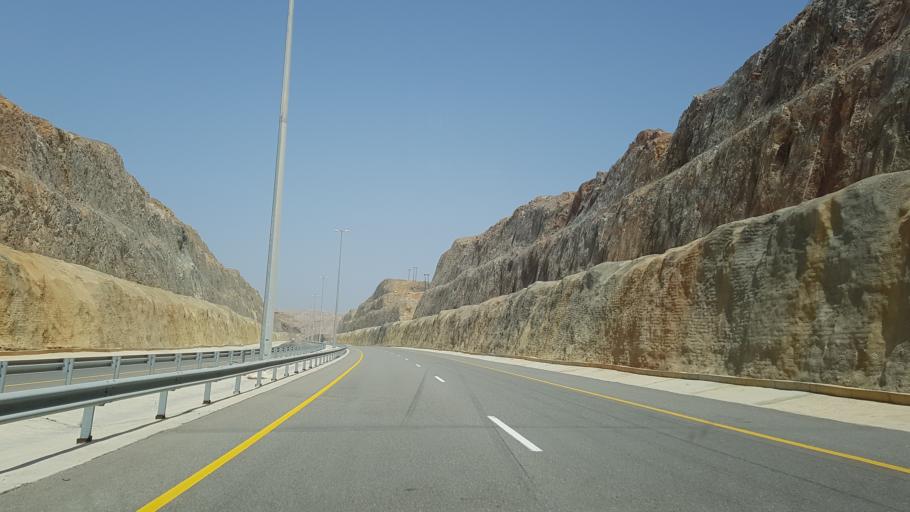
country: OM
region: Muhafazat Masqat
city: Muscat
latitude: 23.1884
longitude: 58.8608
